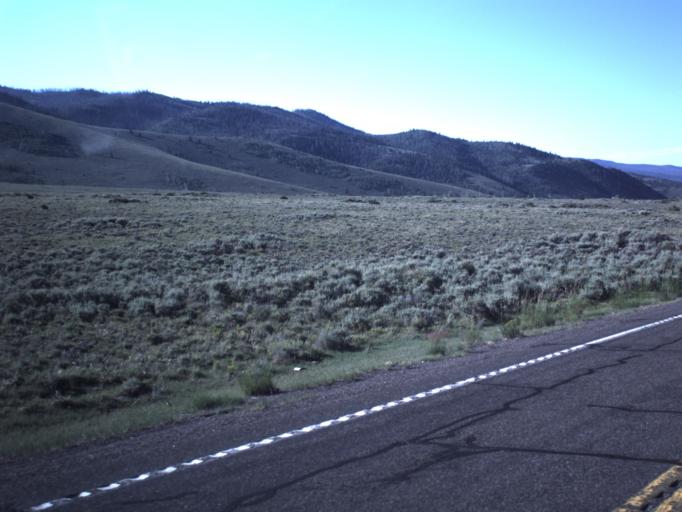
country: US
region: Utah
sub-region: Wayne County
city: Loa
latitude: 38.5529
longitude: -111.5082
